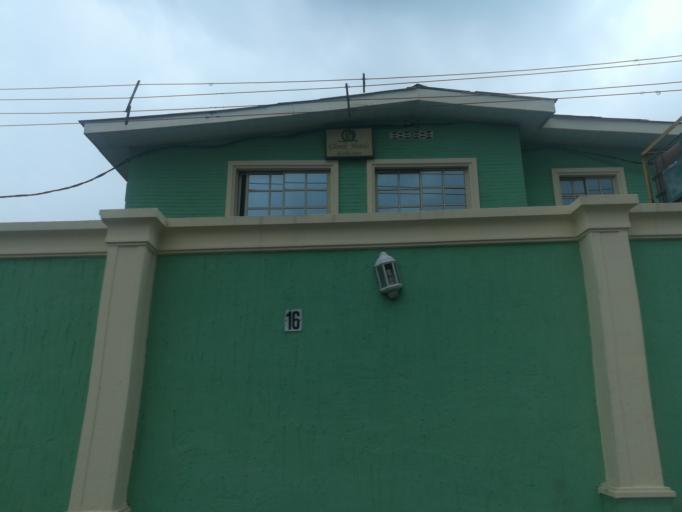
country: NG
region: Lagos
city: Ojota
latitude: 6.5698
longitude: 3.3737
